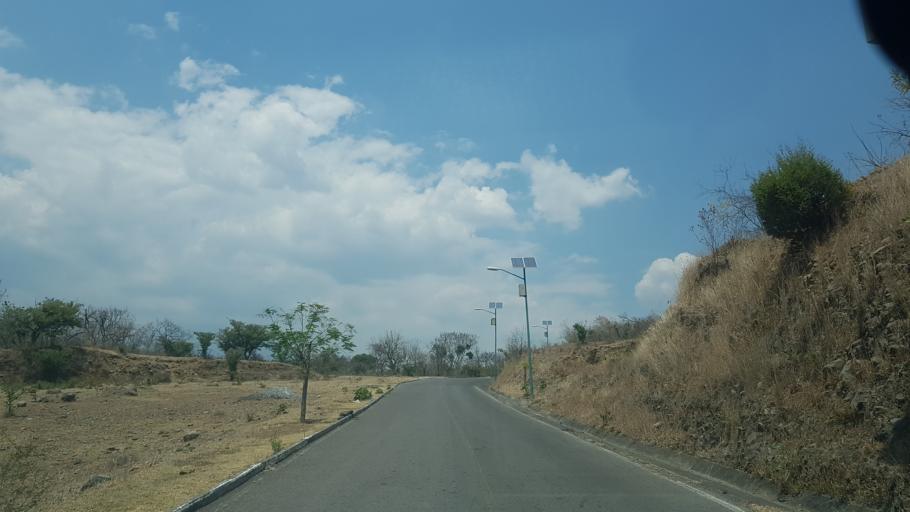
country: MX
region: Puebla
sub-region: Atzitzihuacan
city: Santiago Atzitzihuacan
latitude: 18.8324
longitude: -98.5804
